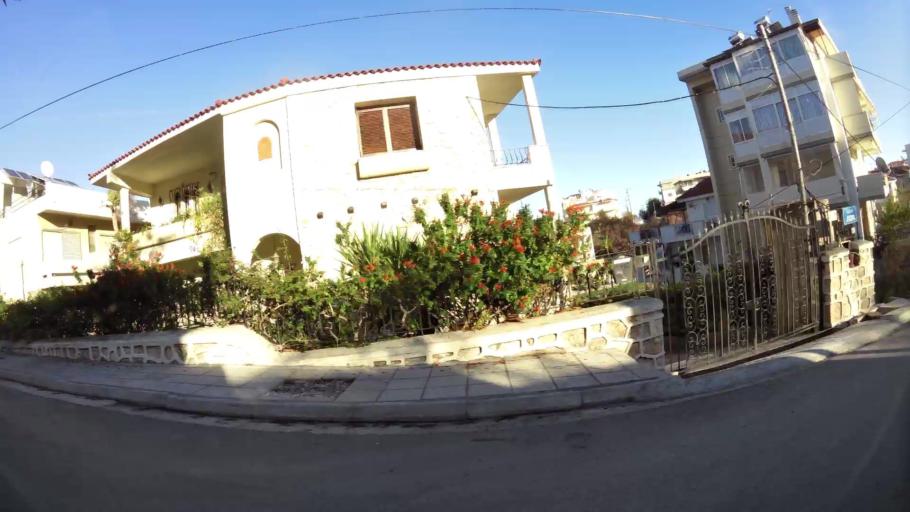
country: GR
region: Attica
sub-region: Nomarchia Anatolikis Attikis
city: Rafina
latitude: 38.0265
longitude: 24.0007
